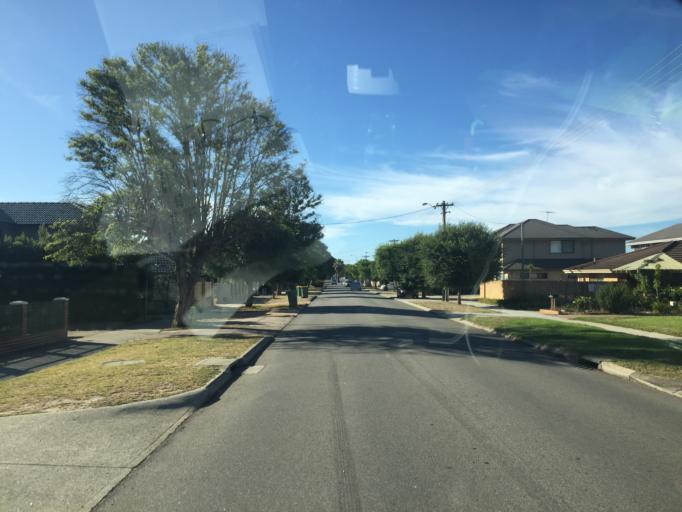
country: AU
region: Western Australia
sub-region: Belmont
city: Rivervale
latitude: -31.9650
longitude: 115.9176
